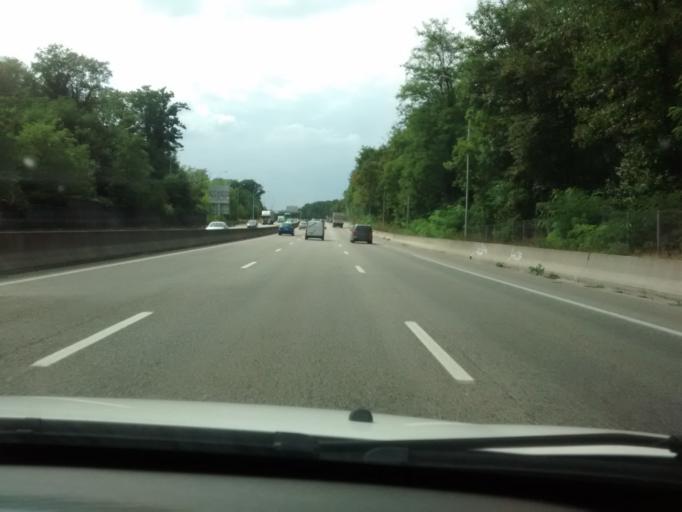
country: FR
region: Ile-de-France
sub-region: Departement des Yvelines
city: Versailles
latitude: 48.7889
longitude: 2.1318
